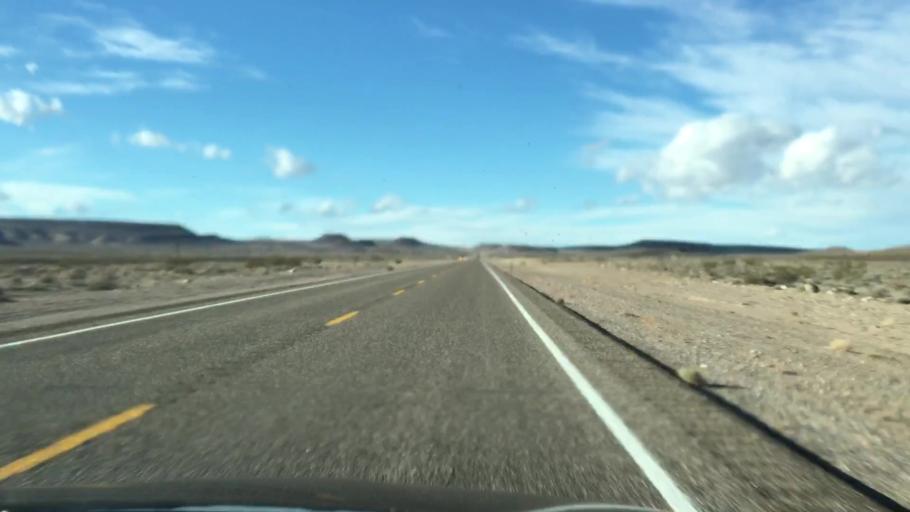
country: US
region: Nevada
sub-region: Esmeralda County
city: Goldfield
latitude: 37.3549
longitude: -117.1102
